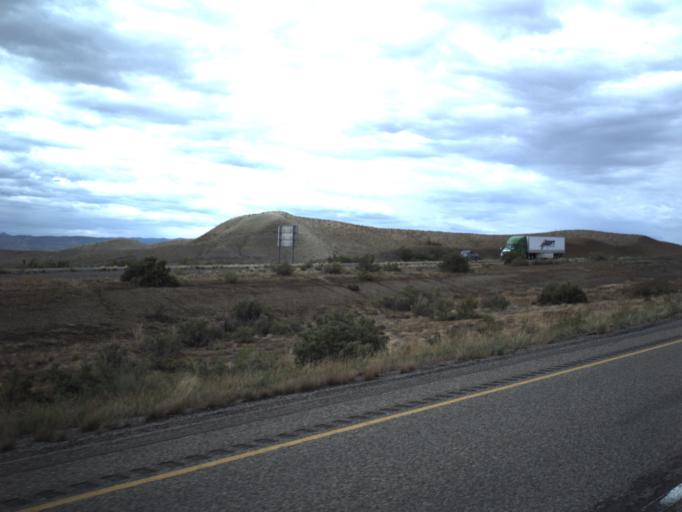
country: US
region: Colorado
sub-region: Mesa County
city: Loma
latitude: 39.1269
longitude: -109.1656
